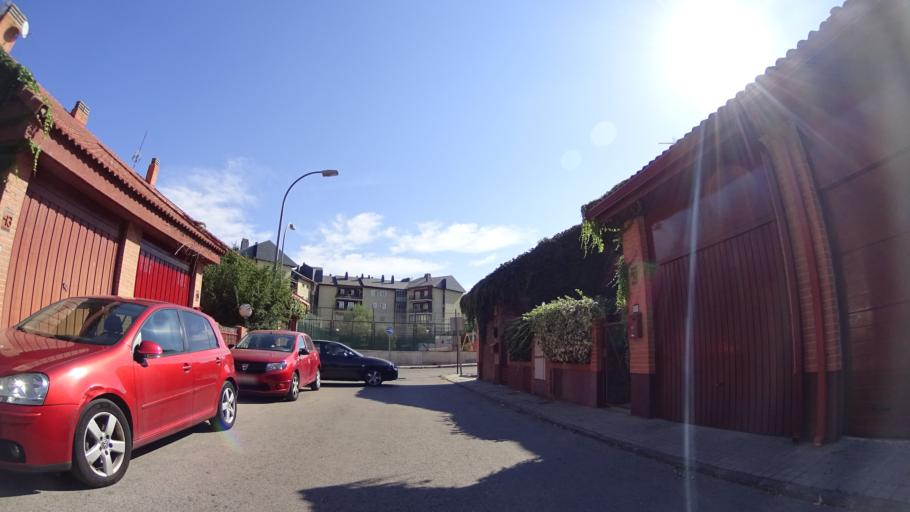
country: ES
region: Madrid
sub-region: Provincia de Madrid
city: Collado-Villalba
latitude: 40.6171
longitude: -4.0052
